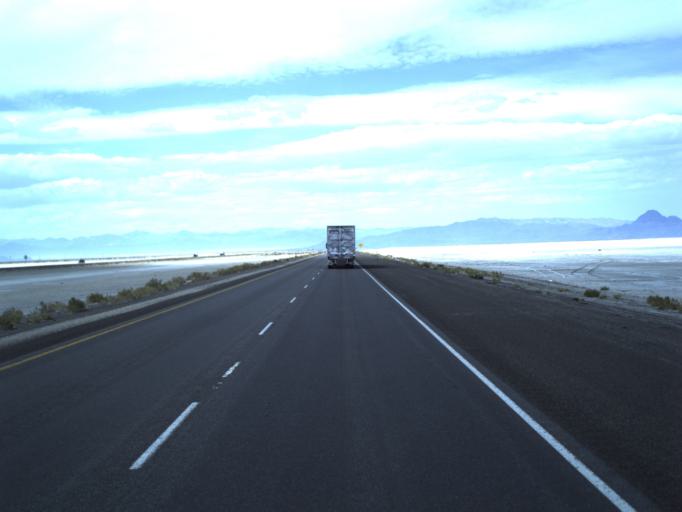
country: US
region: Utah
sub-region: Tooele County
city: Wendover
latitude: 40.7379
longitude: -113.7755
